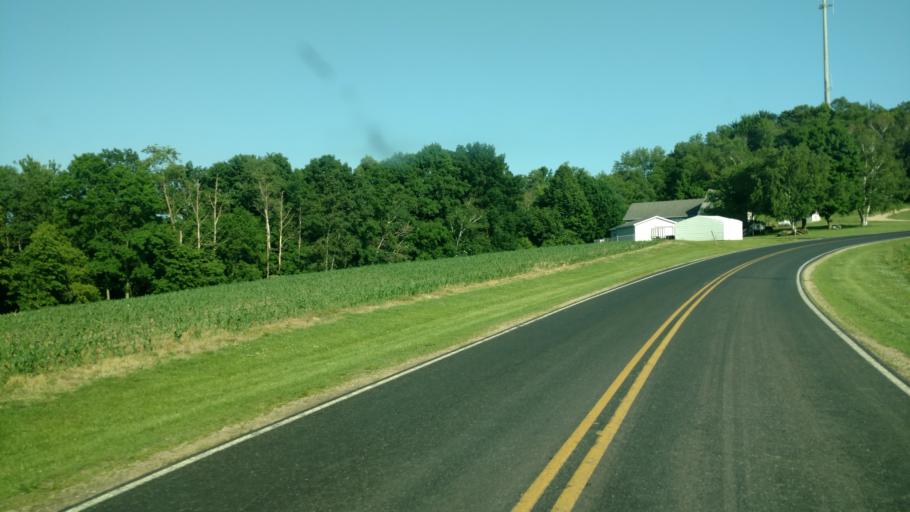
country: US
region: Wisconsin
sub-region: Vernon County
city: Hillsboro
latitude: 43.6643
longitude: -90.3470
